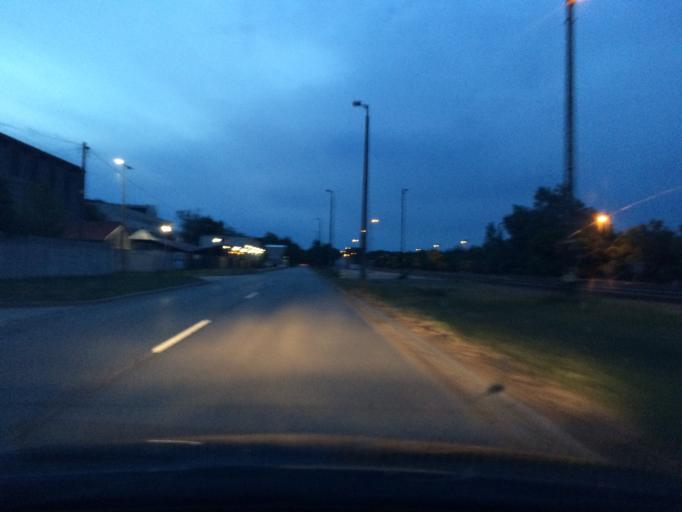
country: HU
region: Szabolcs-Szatmar-Bereg
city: Tiszavasvari
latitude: 47.9420
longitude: 21.3777
